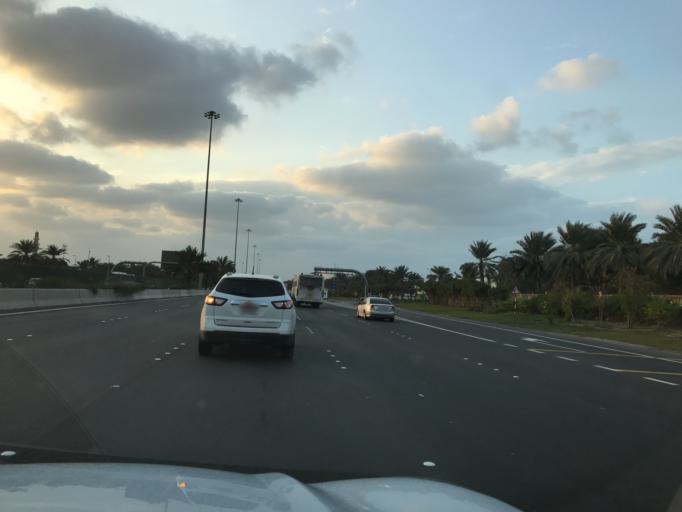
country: AE
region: Abu Dhabi
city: Abu Dhabi
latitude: 24.4183
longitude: 54.4957
